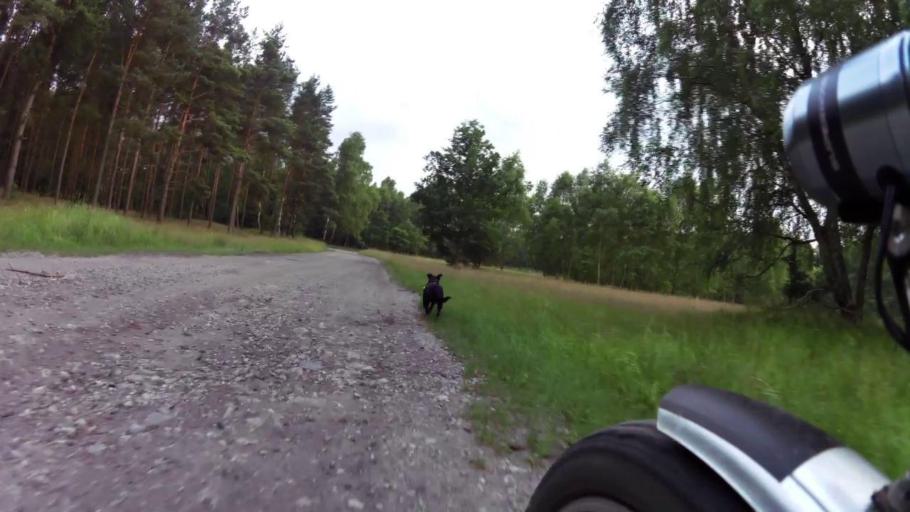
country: PL
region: West Pomeranian Voivodeship
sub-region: Powiat policki
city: Police
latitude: 53.6498
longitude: 14.4945
